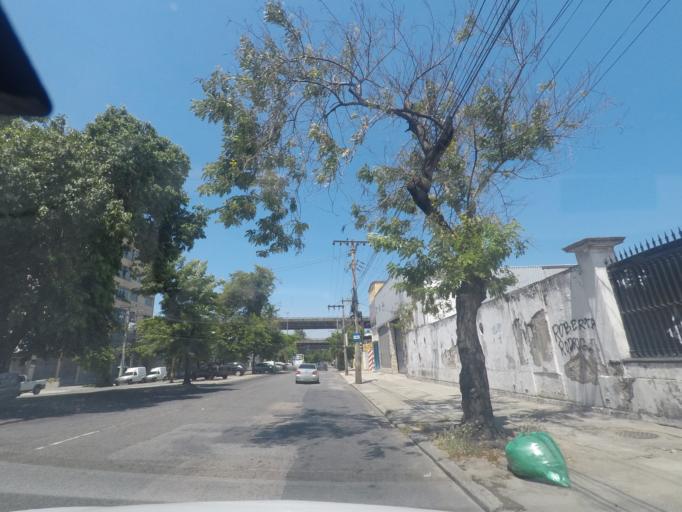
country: BR
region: Rio de Janeiro
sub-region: Rio De Janeiro
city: Rio de Janeiro
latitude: -22.9041
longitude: -43.2164
